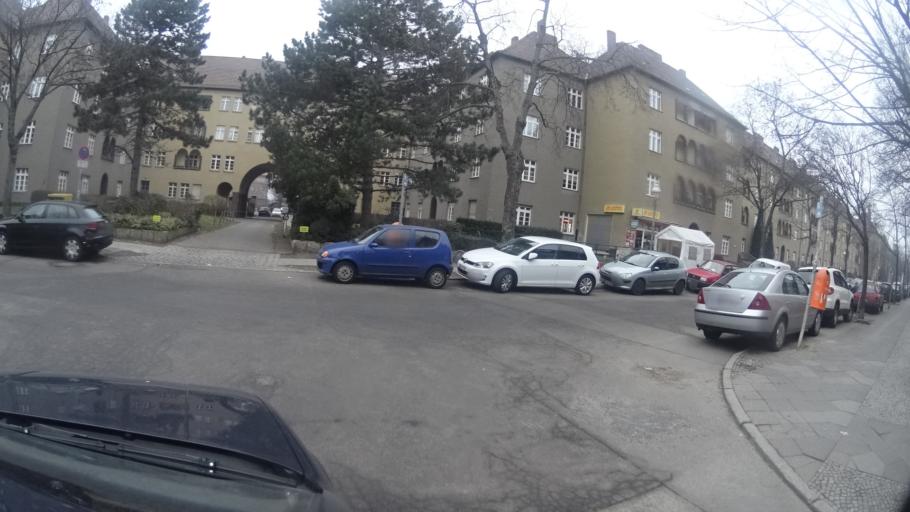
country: DE
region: Berlin
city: Schoneberg Bezirk
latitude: 52.4773
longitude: 13.3715
